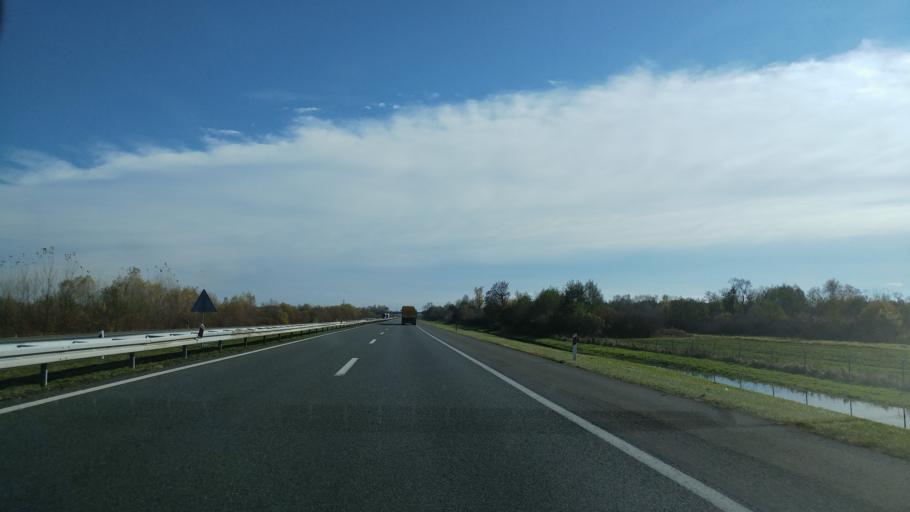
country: HR
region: Brodsko-Posavska
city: Okucani
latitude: 45.2538
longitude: 17.1745
